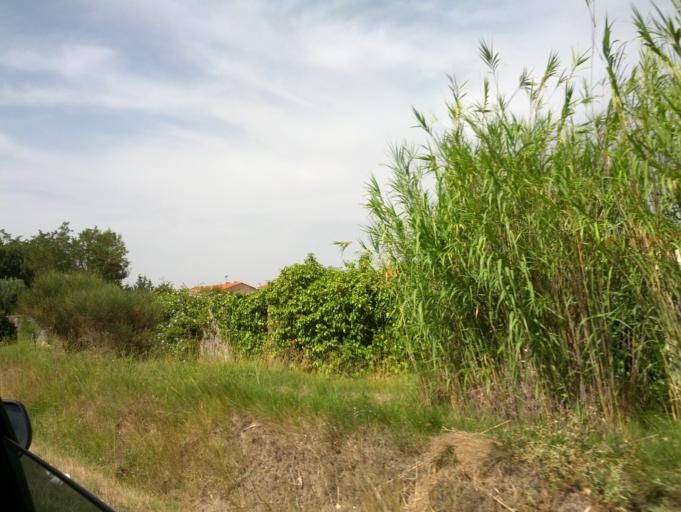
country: FR
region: Languedoc-Roussillon
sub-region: Departement des Pyrenees-Orientales
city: Peyrestortes
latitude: 42.7758
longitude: 2.8290
